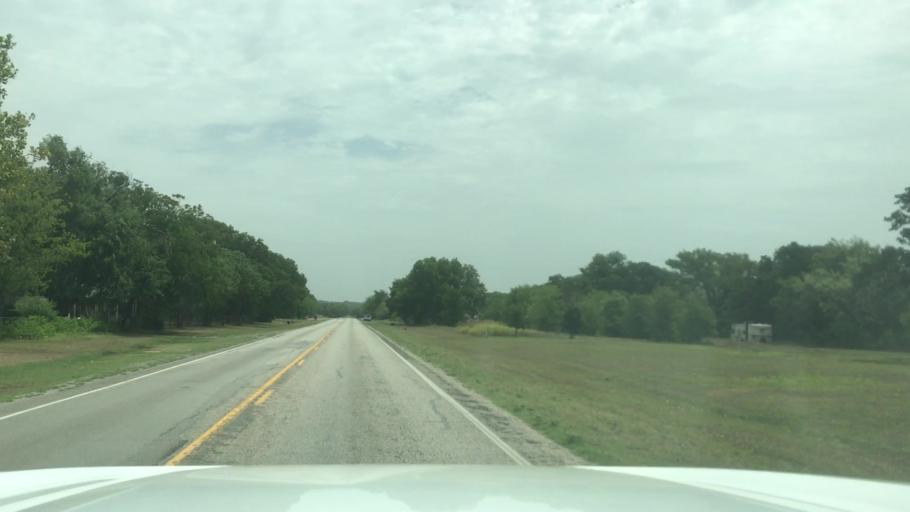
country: US
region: Texas
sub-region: Hamilton County
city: Hico
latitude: 32.0397
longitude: -98.1216
